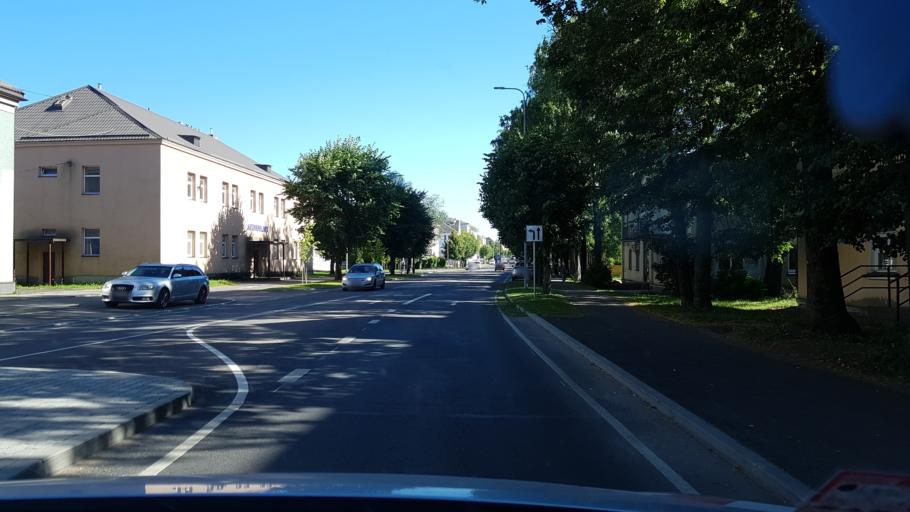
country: EE
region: Ida-Virumaa
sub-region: Kohtla-Jaerve linn
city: Kohtla-Jarve
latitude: 59.4041
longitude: 27.2851
